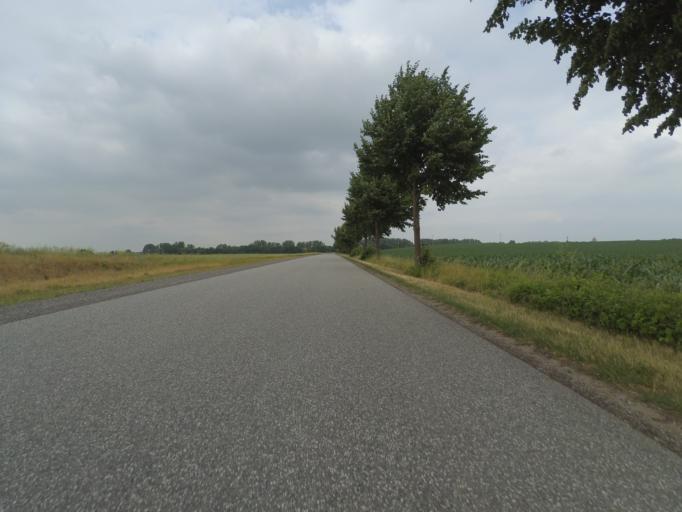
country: DE
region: Mecklenburg-Vorpommern
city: Plau am See
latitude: 53.4525
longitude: 12.2390
